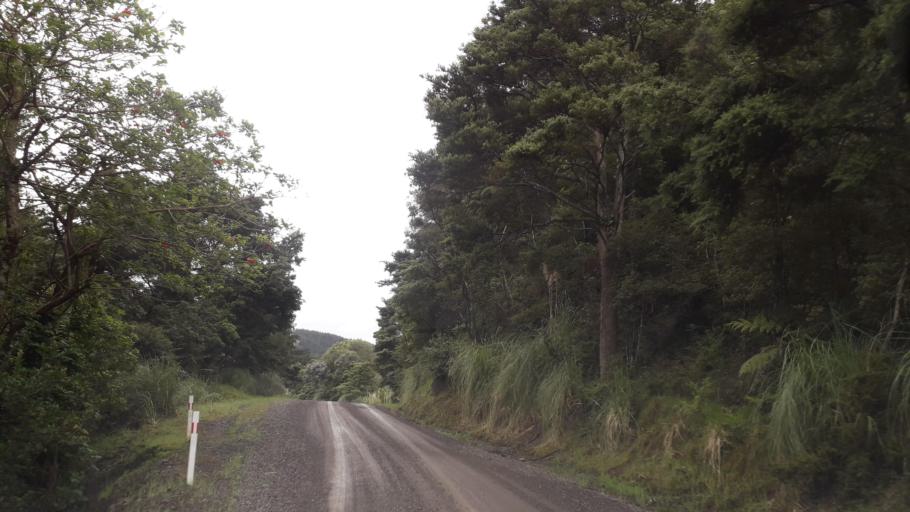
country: NZ
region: Northland
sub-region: Far North District
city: Kaitaia
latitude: -35.3836
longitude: 173.4095
